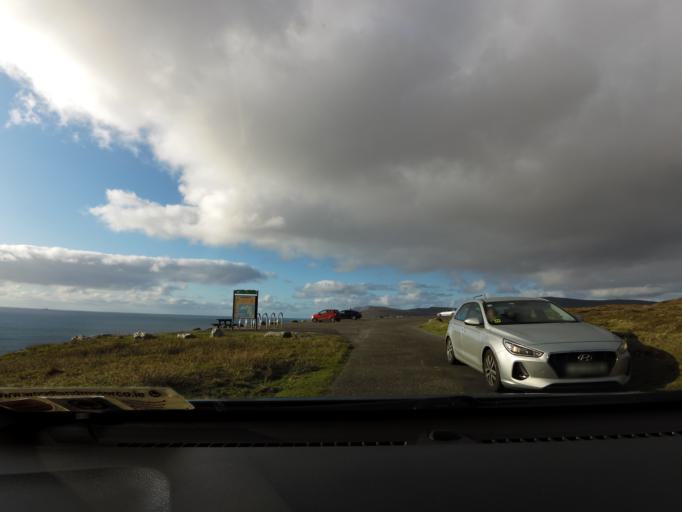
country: IE
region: Connaught
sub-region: Maigh Eo
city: Belmullet
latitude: 53.8985
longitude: -9.9967
